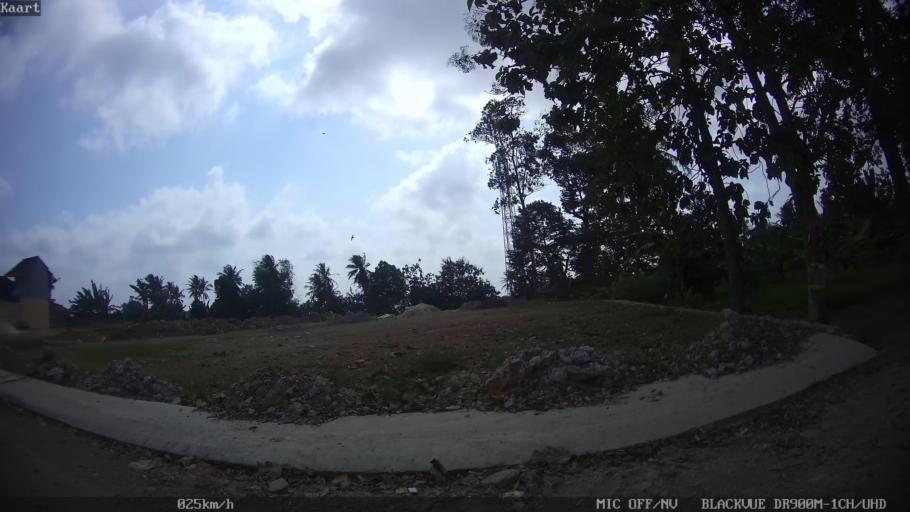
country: ID
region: Lampung
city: Kedaton
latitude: -5.3210
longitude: 105.2895
